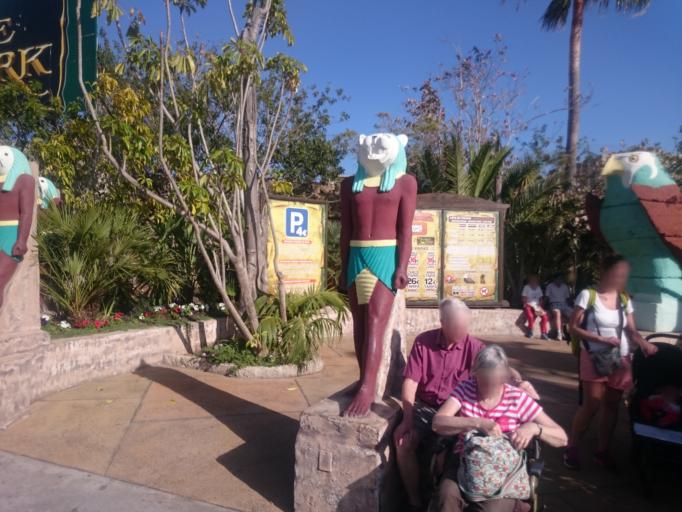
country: ES
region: Canary Islands
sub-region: Provincia de Santa Cruz de Tenerife
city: Arona
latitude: 28.0807
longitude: -16.6946
